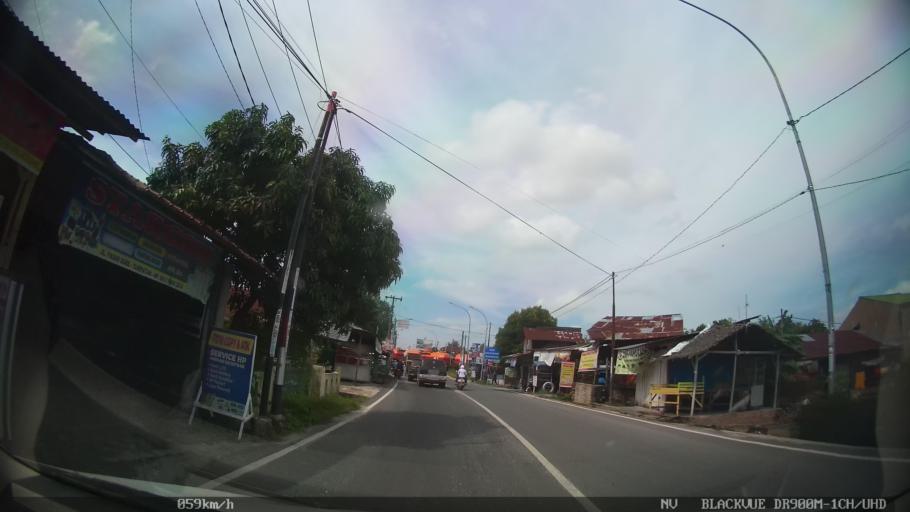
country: ID
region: North Sumatra
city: Percut
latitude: 3.5937
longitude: 98.8593
